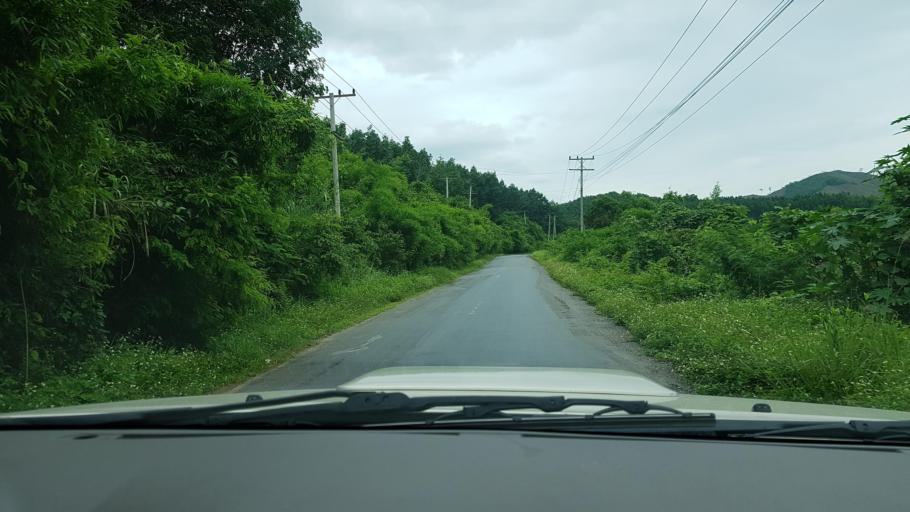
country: LA
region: Loungnamtha
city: Muang Nale
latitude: 20.1975
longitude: 101.5278
